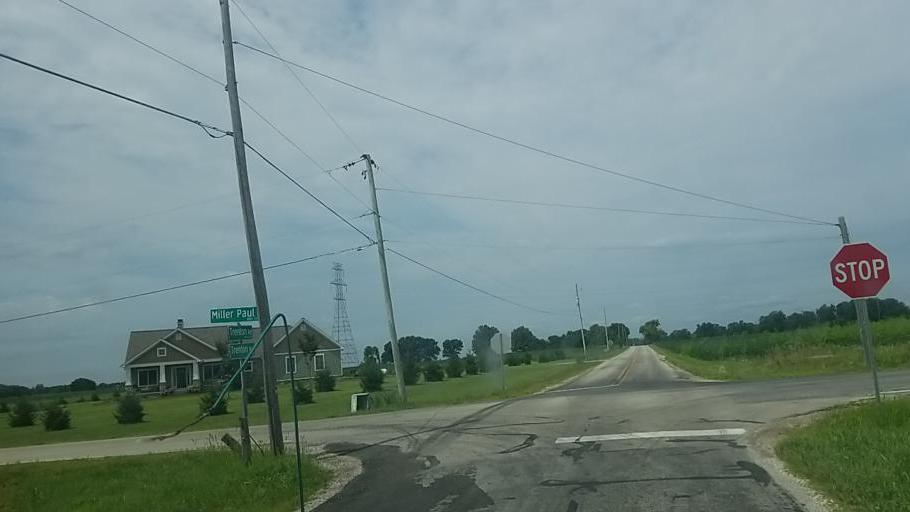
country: US
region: Ohio
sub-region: Delaware County
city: Sunbury
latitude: 40.2042
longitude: -82.8261
